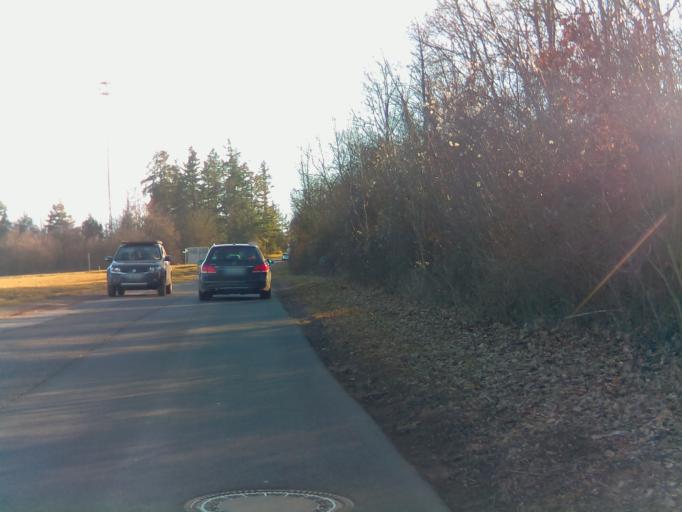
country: DE
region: Rheinland-Pfalz
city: Bad Munster am Stein-Ebernburg
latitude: 49.8181
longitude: 7.8656
